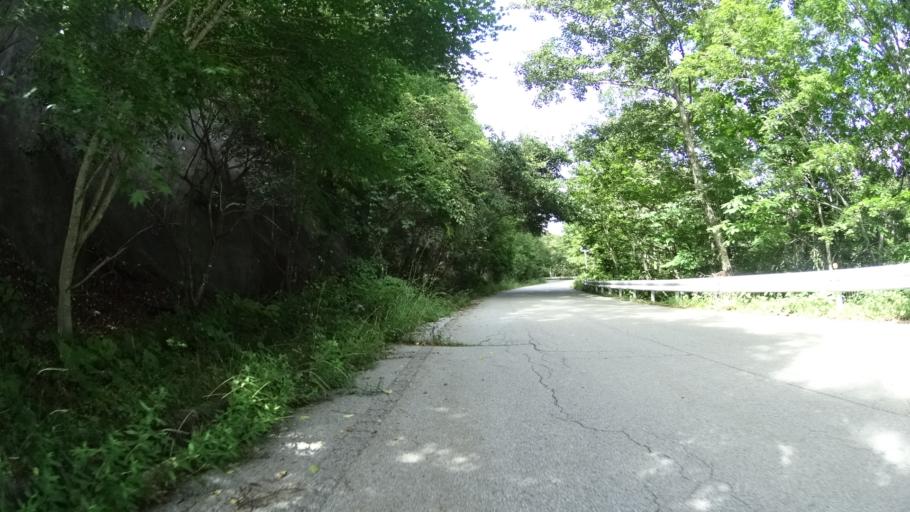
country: JP
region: Yamanashi
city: Nirasaki
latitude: 35.9121
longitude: 138.5416
